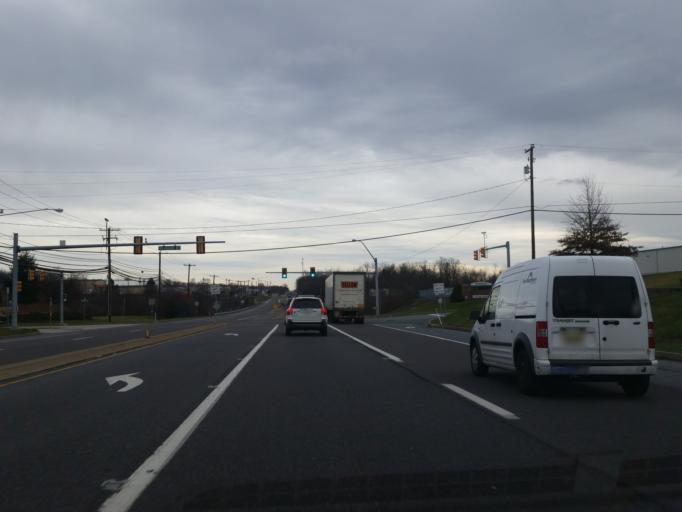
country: US
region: Pennsylvania
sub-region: Dauphin County
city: Linglestown
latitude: 40.3257
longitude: -76.7755
